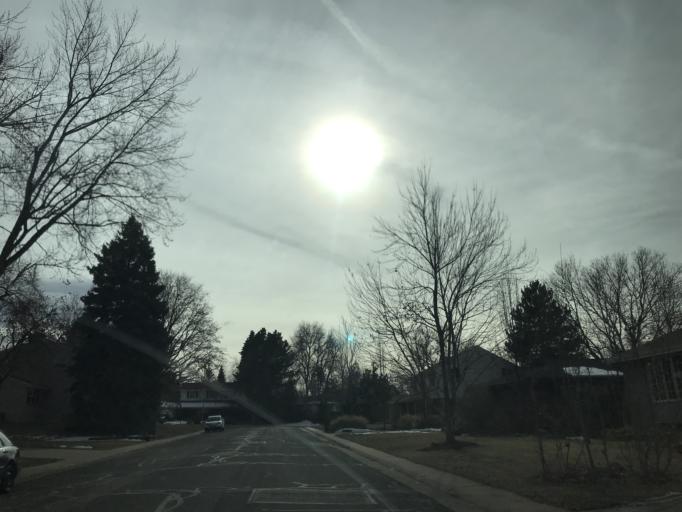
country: US
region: Colorado
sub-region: Arapahoe County
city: Columbine Valley
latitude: 39.5909
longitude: -105.0126
